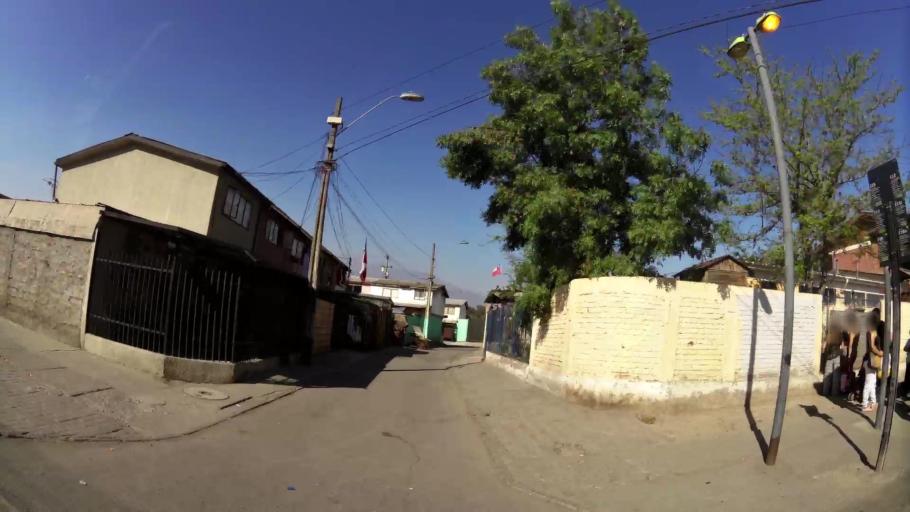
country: CL
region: Santiago Metropolitan
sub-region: Provincia de Santiago
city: La Pintana
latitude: -33.5690
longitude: -70.6094
